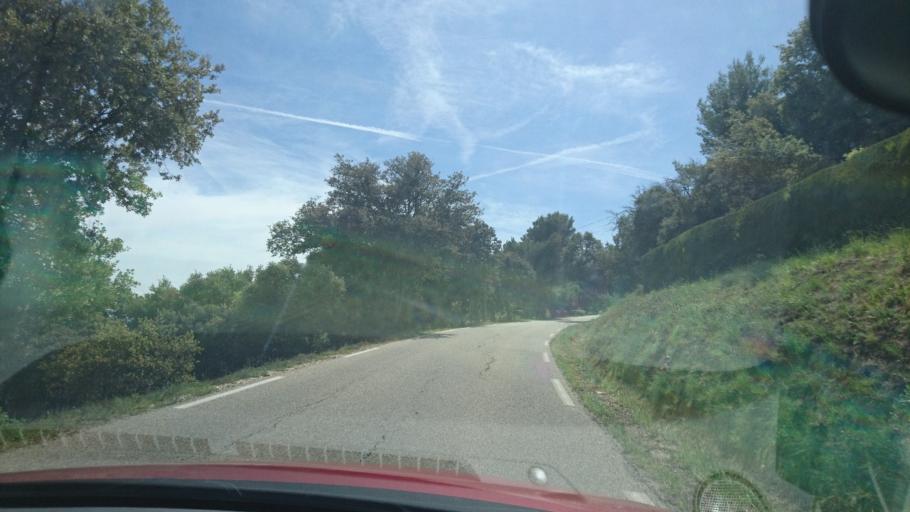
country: FR
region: Provence-Alpes-Cote d'Azur
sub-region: Departement du Vaucluse
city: Bedoin
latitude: 44.1401
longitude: 5.1518
